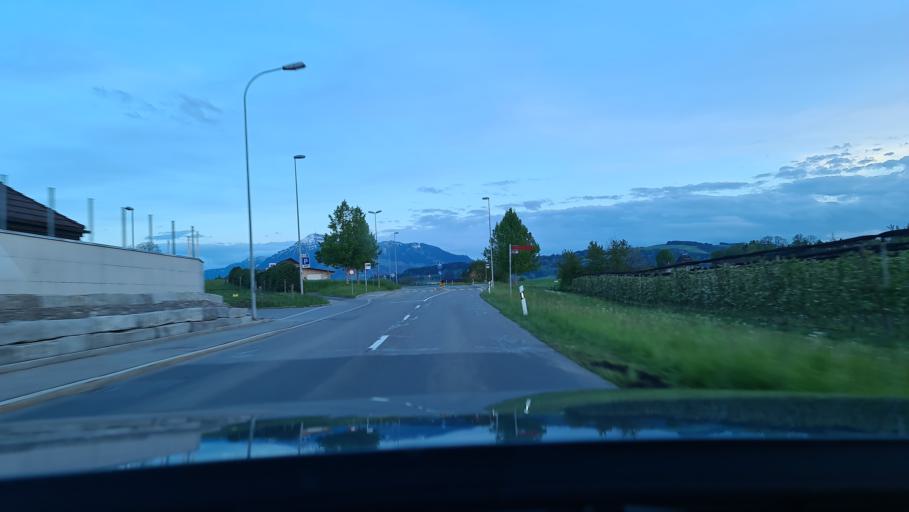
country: CH
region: Zug
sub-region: Zug
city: Hunenberg
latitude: 47.1702
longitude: 8.4278
